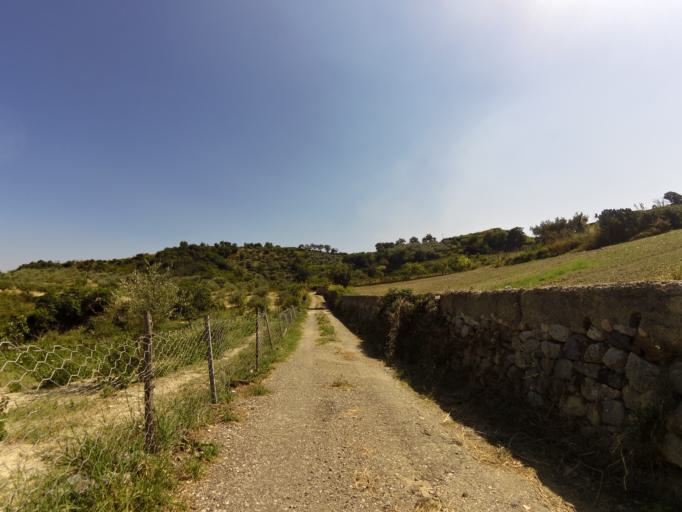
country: IT
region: Calabria
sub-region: Provincia di Reggio Calabria
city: Pazzano
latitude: 38.4645
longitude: 16.4543
